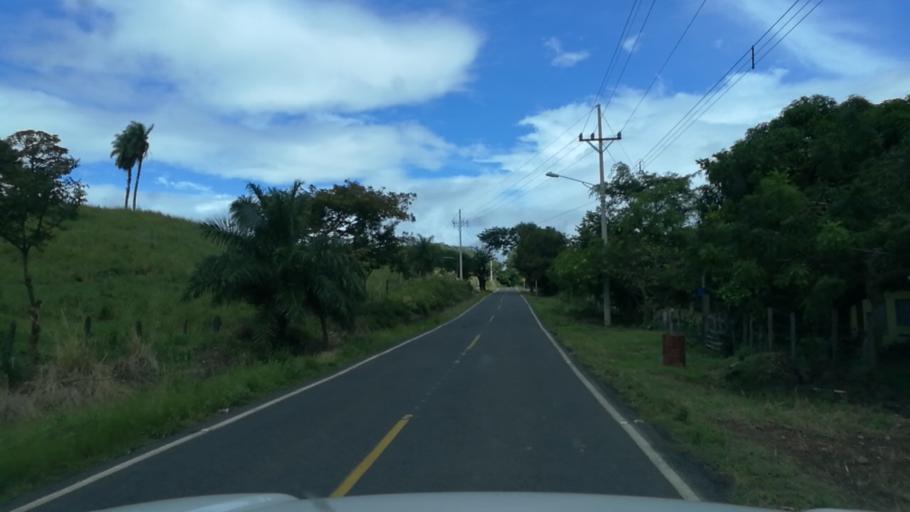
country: CR
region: Guanacaste
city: Fortuna
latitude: 10.6500
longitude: -85.2342
